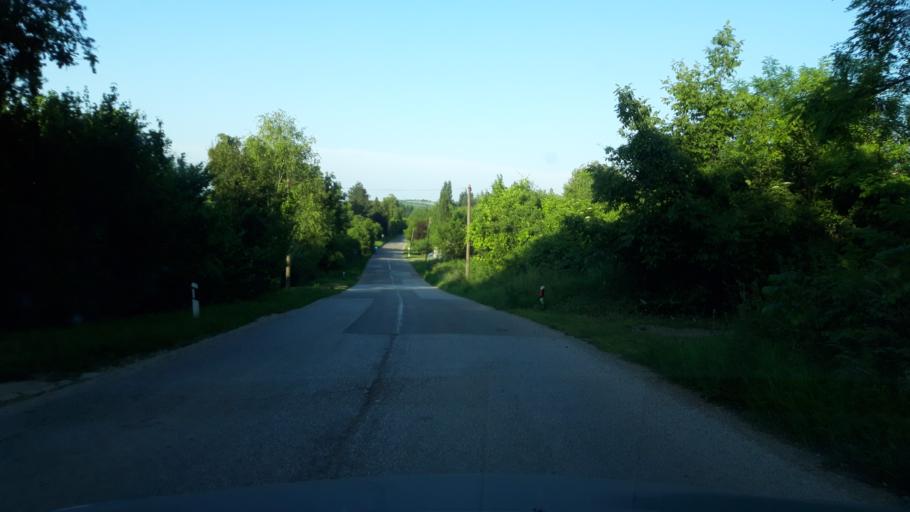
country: RS
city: Glozan
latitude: 45.2055
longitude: 19.5817
